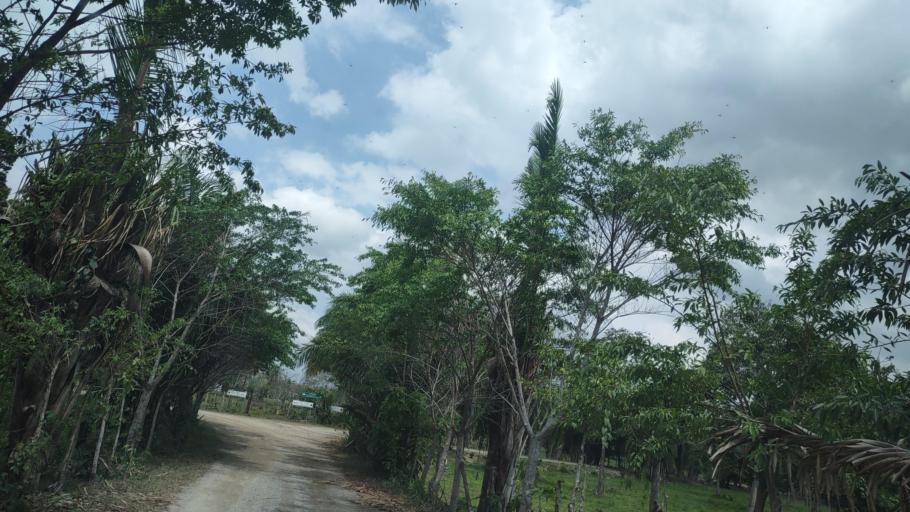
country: MX
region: Veracruz
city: Las Choapas
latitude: 17.9642
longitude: -94.1244
